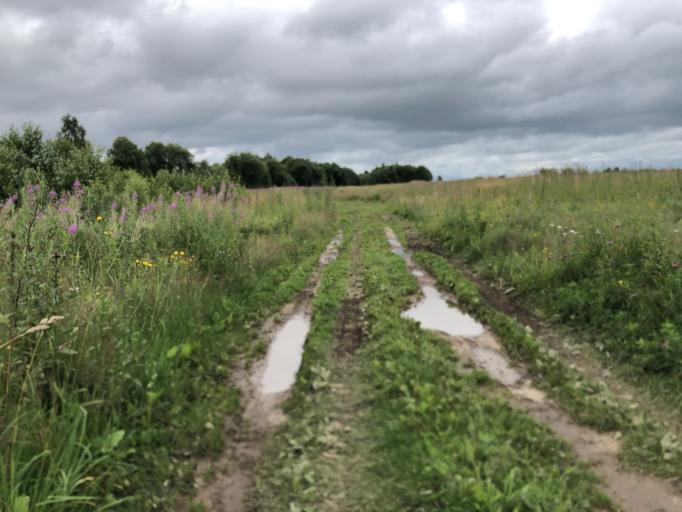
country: RU
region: Tverskaya
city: Rzhev
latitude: 56.2399
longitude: 34.3799
